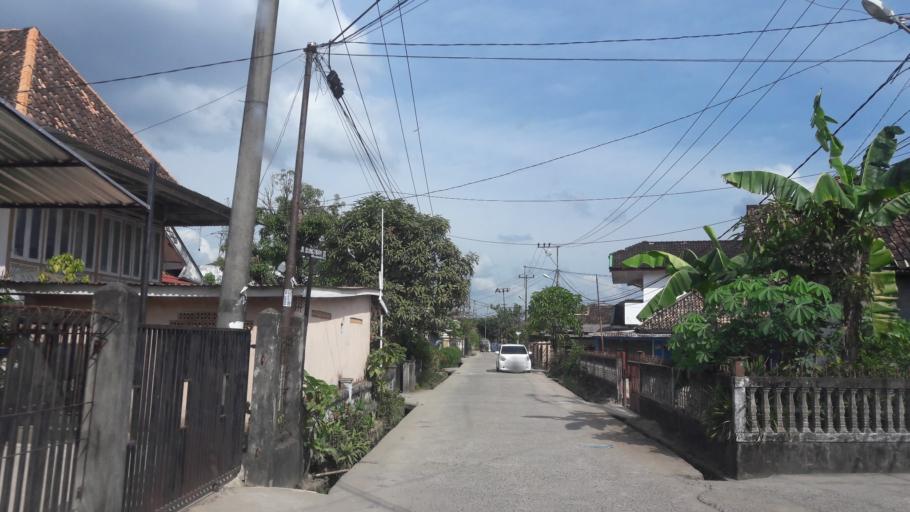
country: ID
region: South Sumatra
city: Plaju
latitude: -3.0028
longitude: 104.7695
